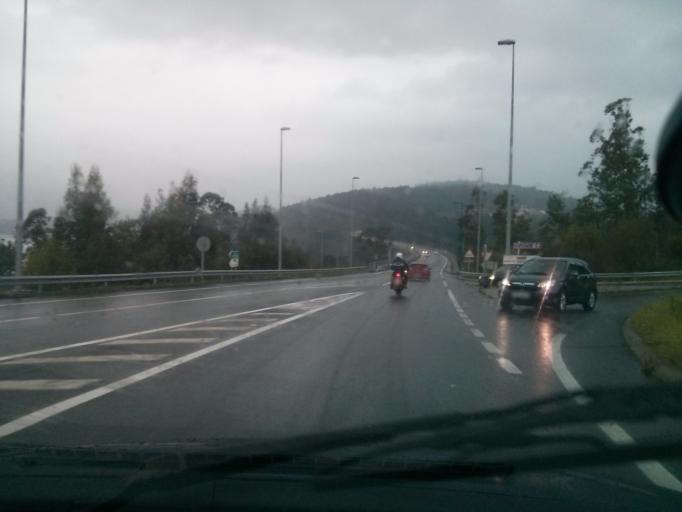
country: ES
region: Galicia
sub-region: Provincia da Coruna
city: Noia
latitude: 42.8122
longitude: -8.8846
